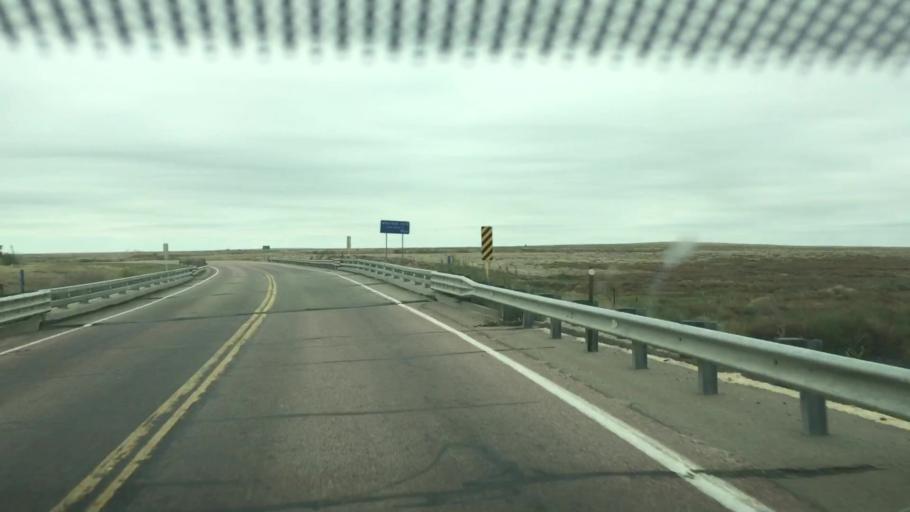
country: US
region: Kansas
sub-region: Hamilton County
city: Syracuse
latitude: 38.0496
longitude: -102.0491
